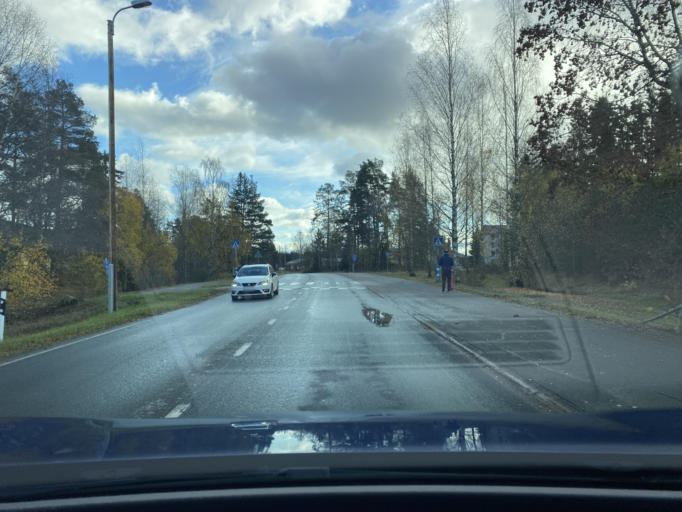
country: FI
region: Varsinais-Suomi
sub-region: Loimaa
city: Aura
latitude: 60.7209
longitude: 22.6008
